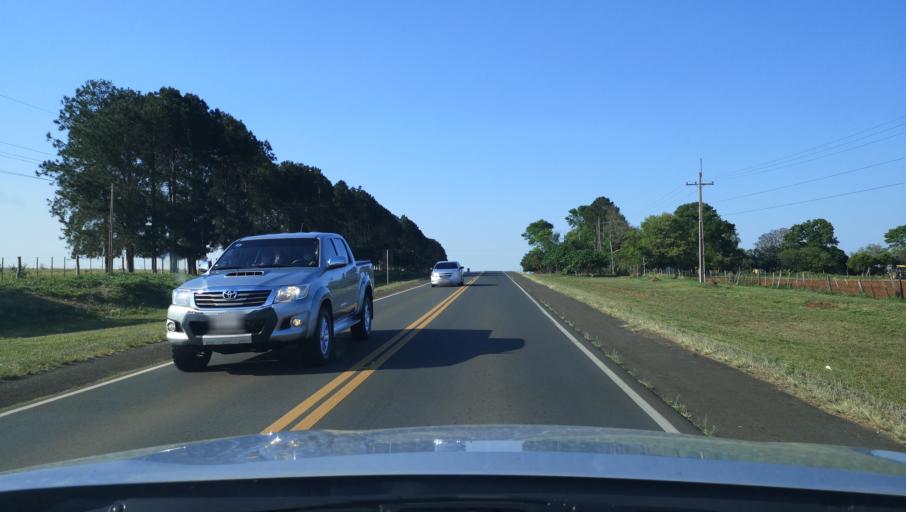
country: PY
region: Misiones
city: Santa Maria
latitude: -26.8425
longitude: -57.0369
